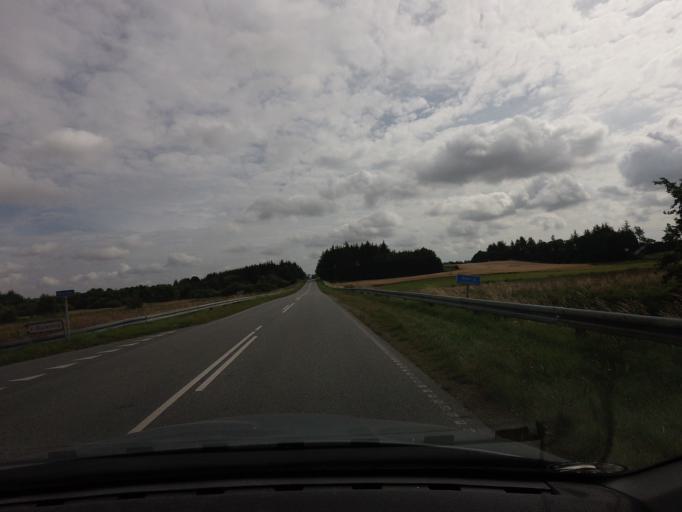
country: DK
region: North Denmark
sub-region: Bronderslev Kommune
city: Dronninglund
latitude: 57.2835
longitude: 10.2900
